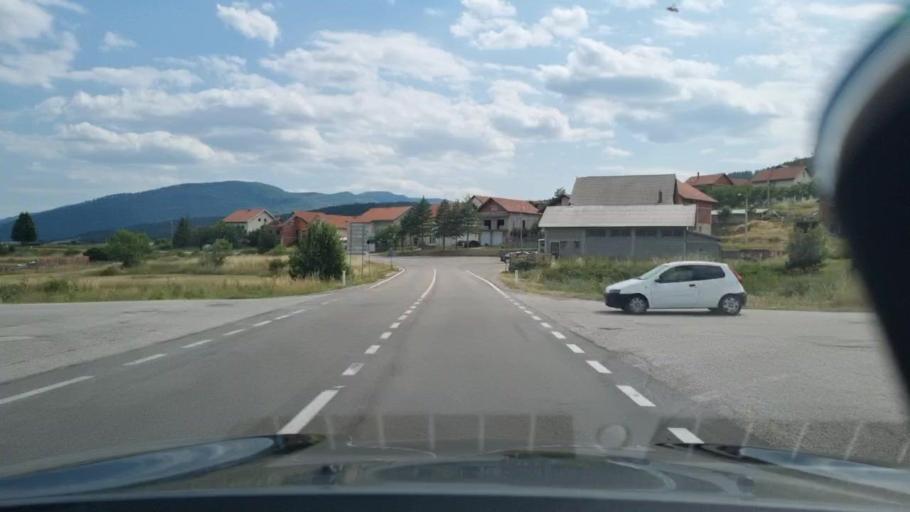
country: BA
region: Federation of Bosnia and Herzegovina
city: Bosansko Grahovo
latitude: 44.1748
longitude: 16.3719
